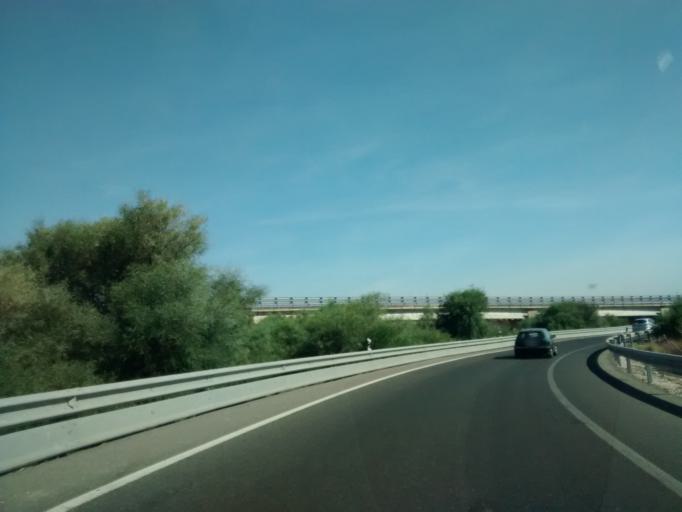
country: ES
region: Andalusia
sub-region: Provincia de Cadiz
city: San Fernando
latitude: 36.4673
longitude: -6.1649
